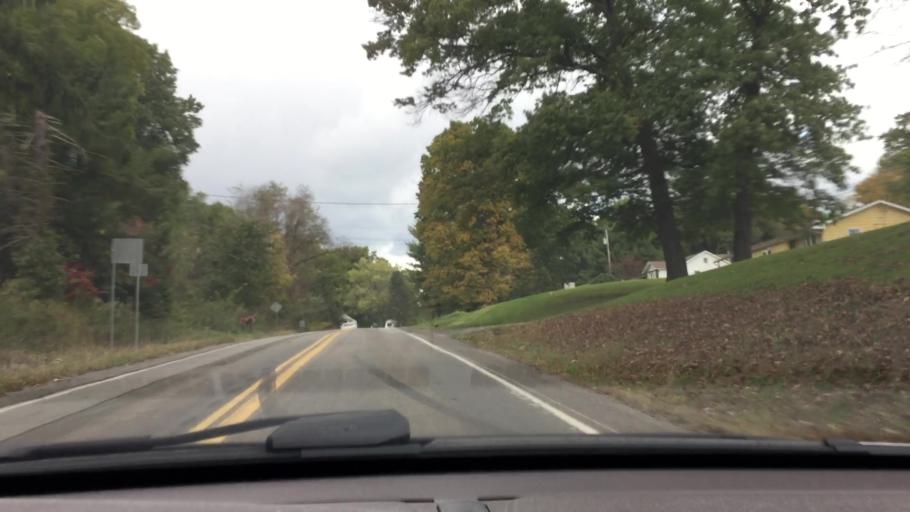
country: US
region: Pennsylvania
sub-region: Lawrence County
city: Oakwood
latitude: 41.0219
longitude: -80.4400
